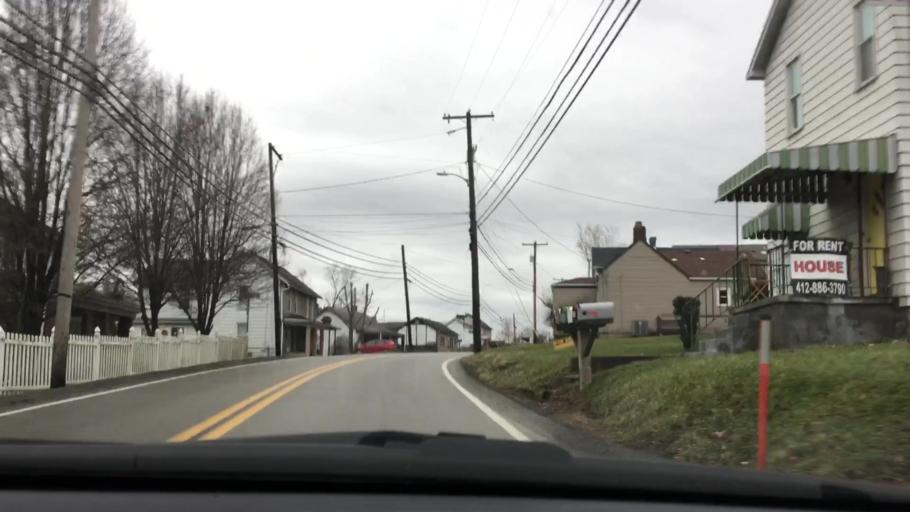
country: US
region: Pennsylvania
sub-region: Washington County
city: Gastonville
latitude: 40.2482
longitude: -80.0212
